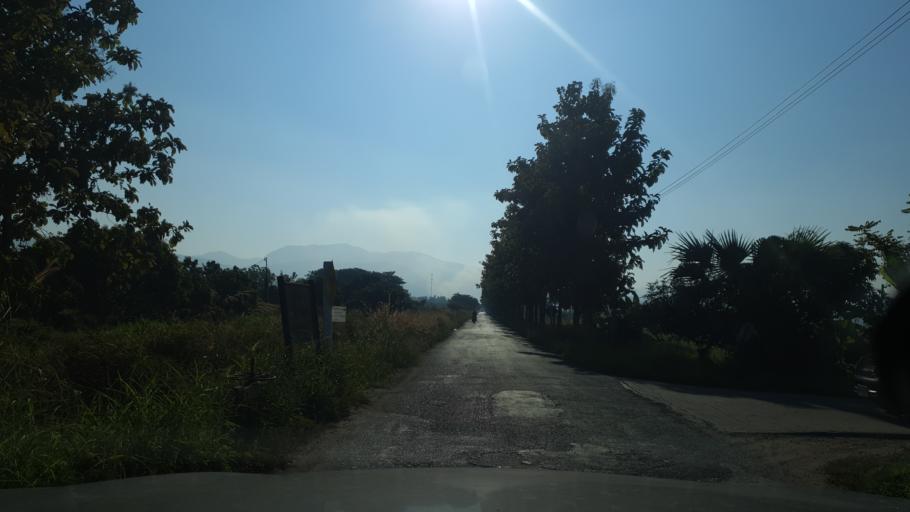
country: TH
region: Chiang Mai
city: San Kamphaeng
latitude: 18.6985
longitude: 99.1469
